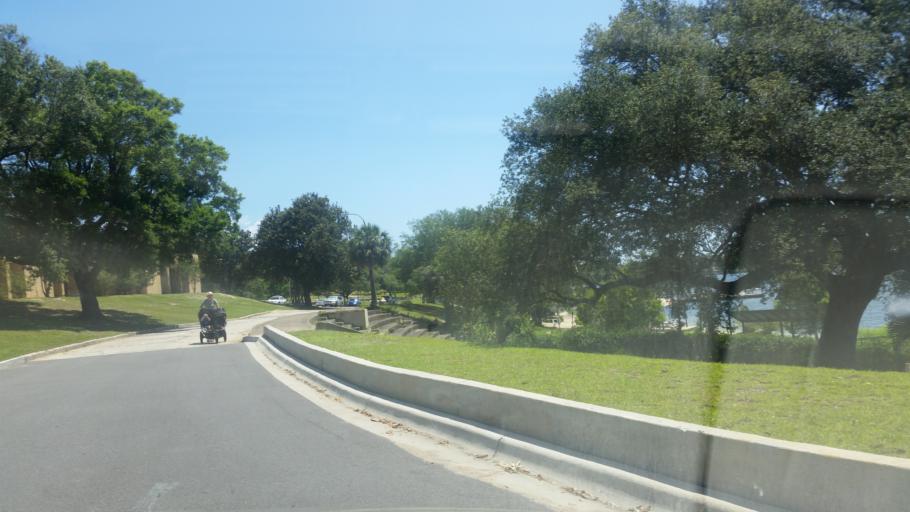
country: US
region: Florida
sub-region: Escambia County
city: East Pensacola Heights
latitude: 30.4307
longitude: -87.1918
